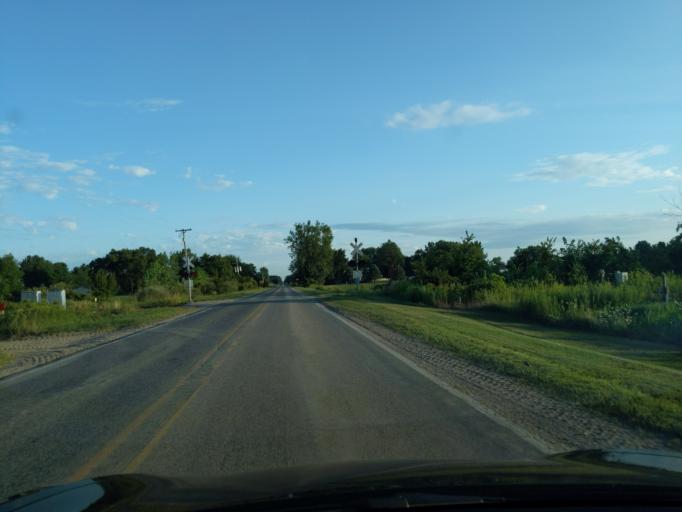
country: US
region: Michigan
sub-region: Gratiot County
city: Breckenridge
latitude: 43.4122
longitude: -84.3699
